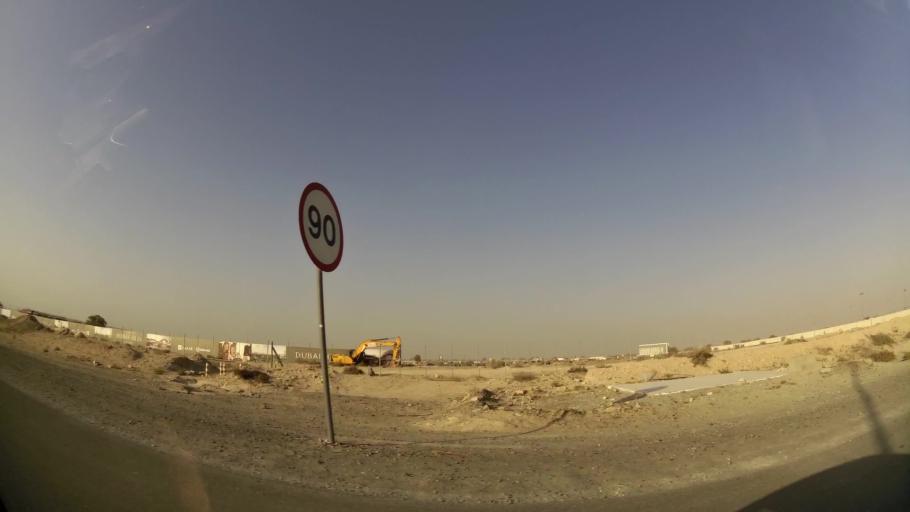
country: AE
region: Dubai
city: Dubai
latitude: 25.0871
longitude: 55.2481
